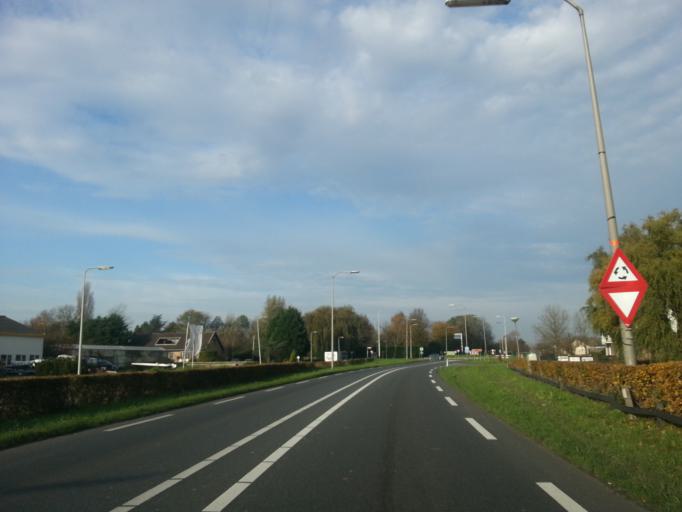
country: NL
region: South Holland
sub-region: Gemeente Capelle aan den IJssel
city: Capelle aan den IJssel
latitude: 51.9879
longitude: 4.6022
